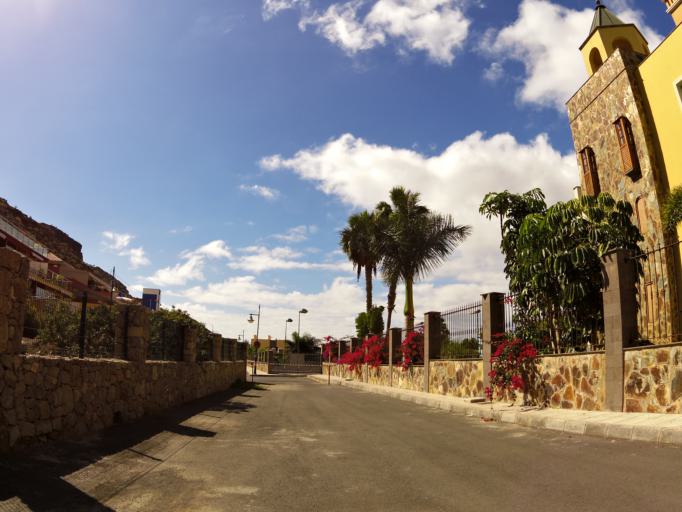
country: ES
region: Canary Islands
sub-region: Provincia de Las Palmas
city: Puerto Rico
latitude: 27.8214
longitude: -15.7605
